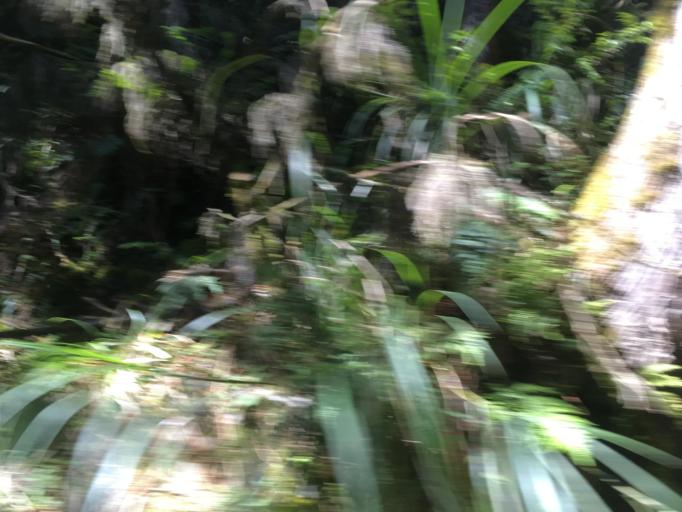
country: TW
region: Taiwan
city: Daxi
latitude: 24.5871
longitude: 121.4113
